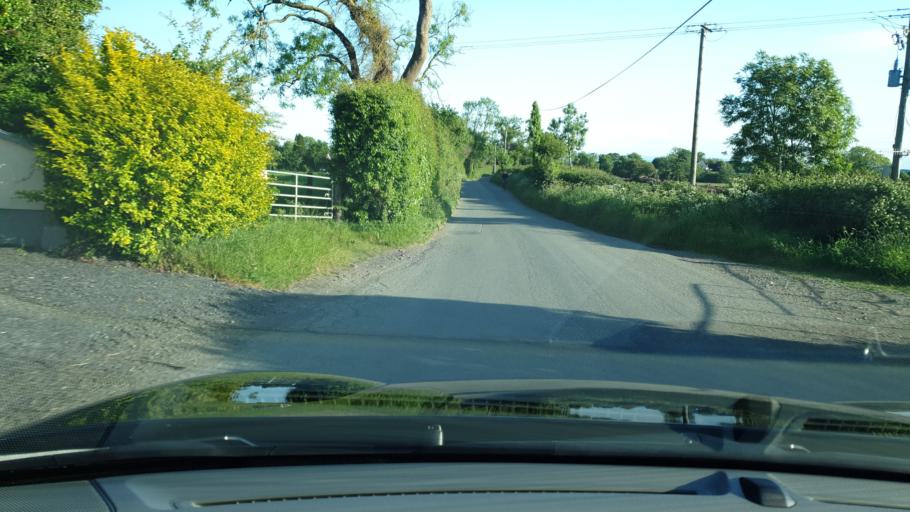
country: IE
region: Leinster
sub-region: Fingal County
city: Swords
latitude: 53.5127
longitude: -6.2354
